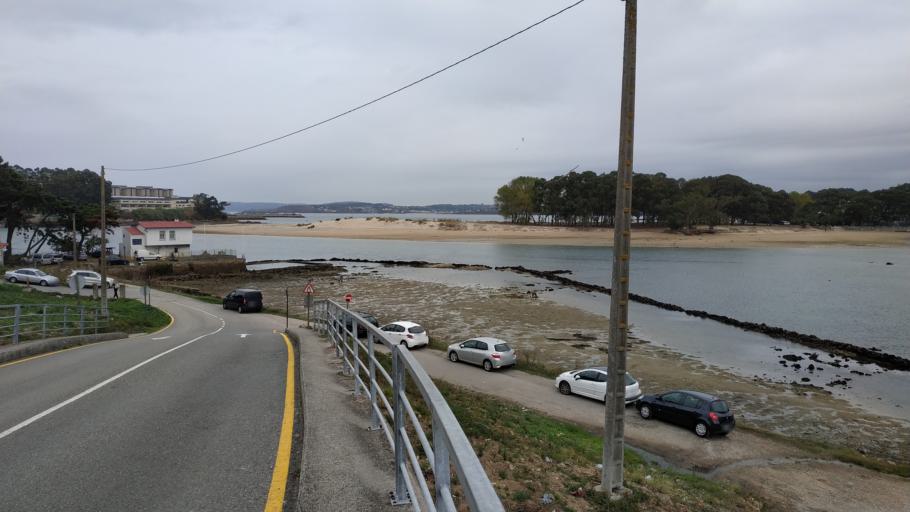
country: ES
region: Galicia
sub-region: Provincia da Coruna
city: A Coruna
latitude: 43.3379
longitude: -8.3866
